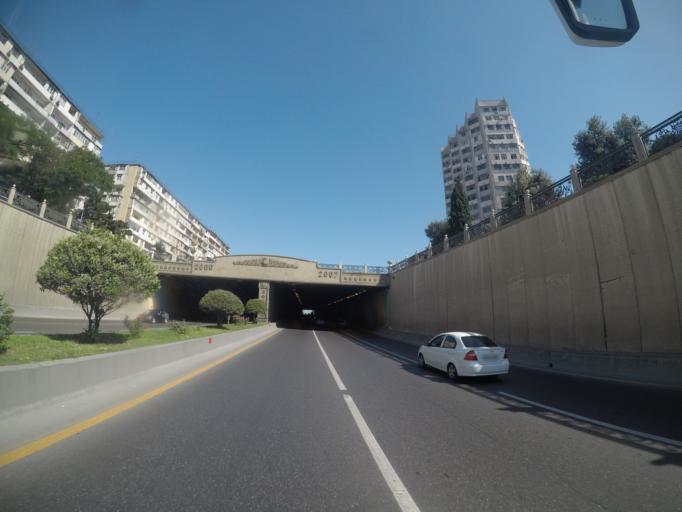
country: AZ
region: Baki
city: Bilajari
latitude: 40.4095
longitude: 49.8046
